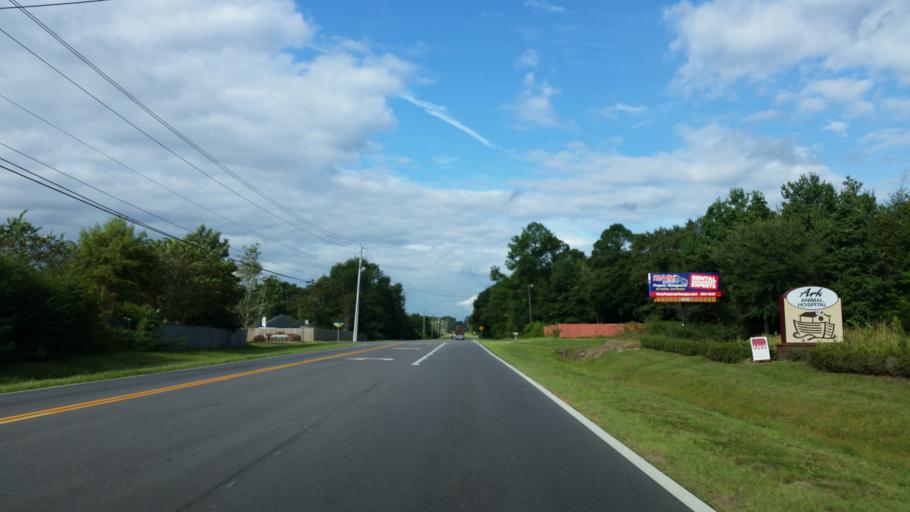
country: US
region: Florida
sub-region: Santa Rosa County
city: Wallace
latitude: 30.6459
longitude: -87.1706
